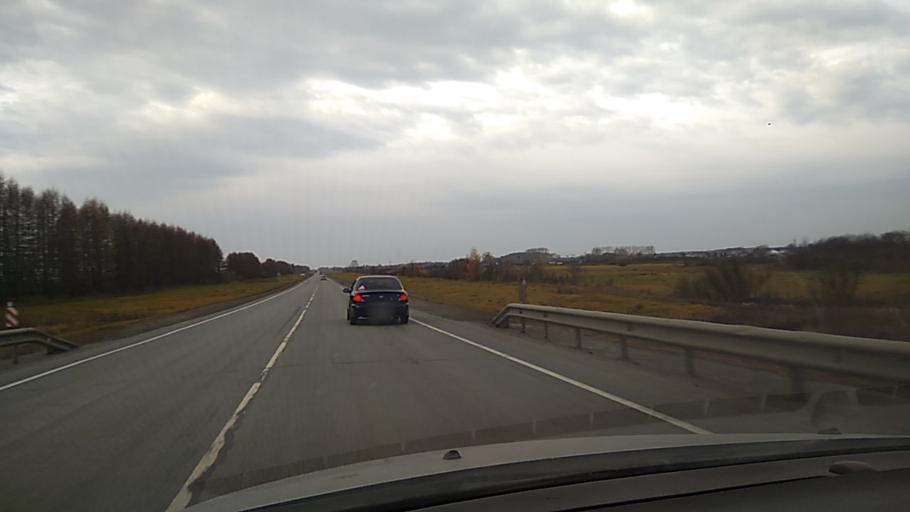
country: RU
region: Sverdlovsk
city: Troitskiy
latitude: 57.0814
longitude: 63.6495
